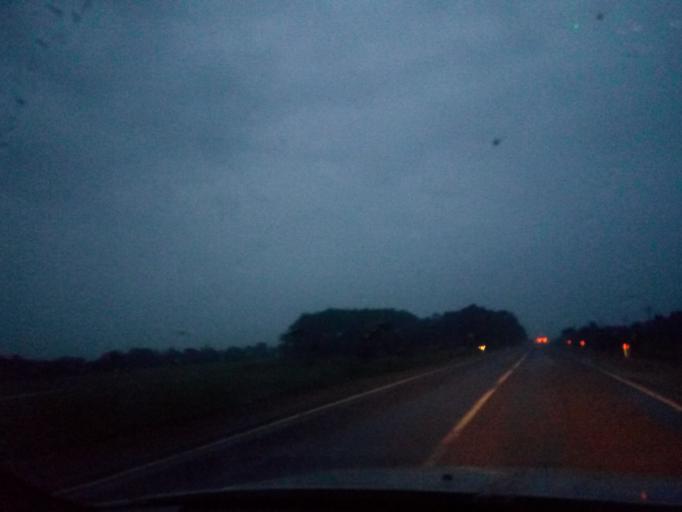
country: RU
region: Primorskiy
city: Dal'nerechensk
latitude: 45.9043
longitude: 133.7512
